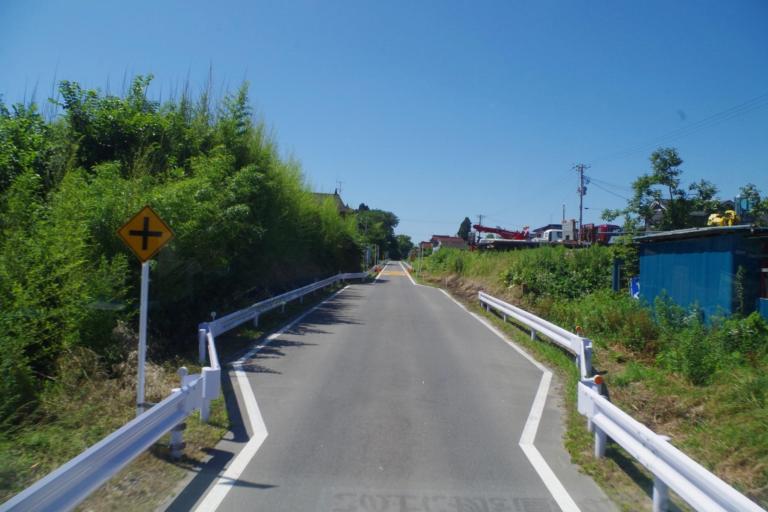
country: JP
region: Iwate
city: Ofunato
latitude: 38.8628
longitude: 141.5842
